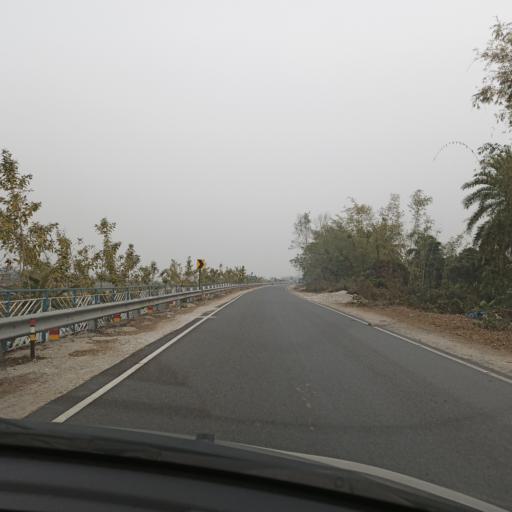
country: IN
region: West Bengal
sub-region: Jalpaiguri
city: Odlabari
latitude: 26.7366
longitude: 88.5752
